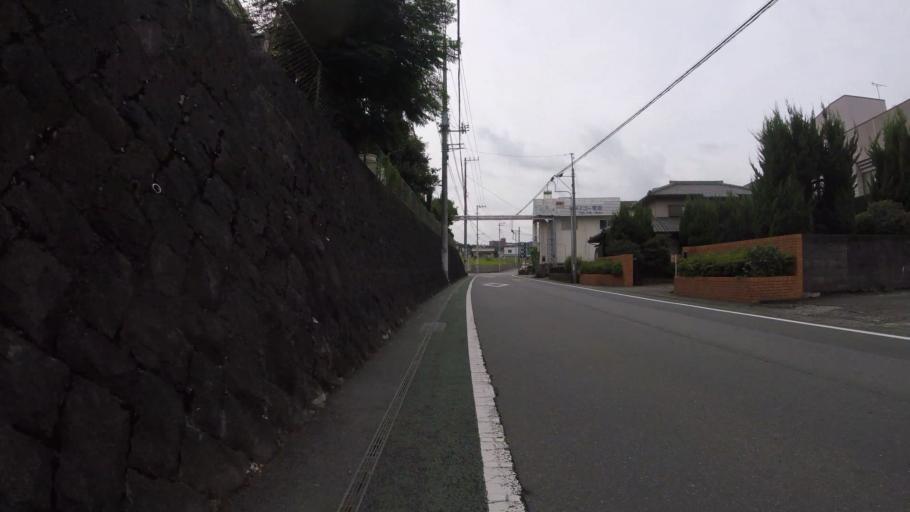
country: JP
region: Shizuoka
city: Mishima
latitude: 35.0071
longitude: 138.9461
